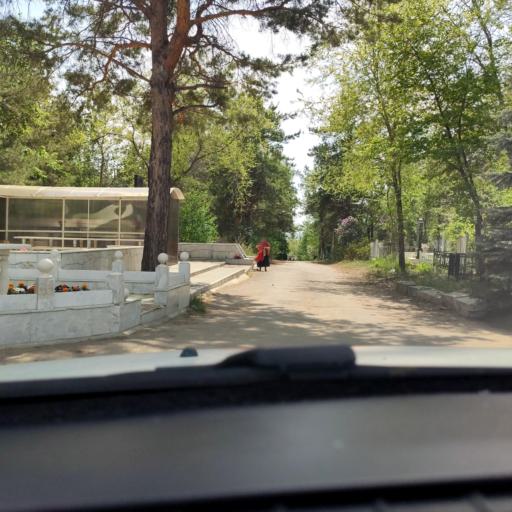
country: RU
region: Samara
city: Samara
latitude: 53.1155
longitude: 50.2328
